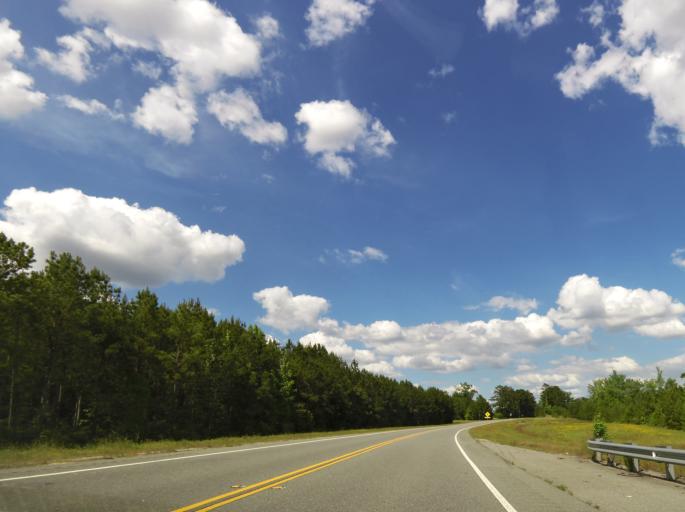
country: US
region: Georgia
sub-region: Treutlen County
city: Soperton
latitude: 32.3114
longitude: -82.6897
